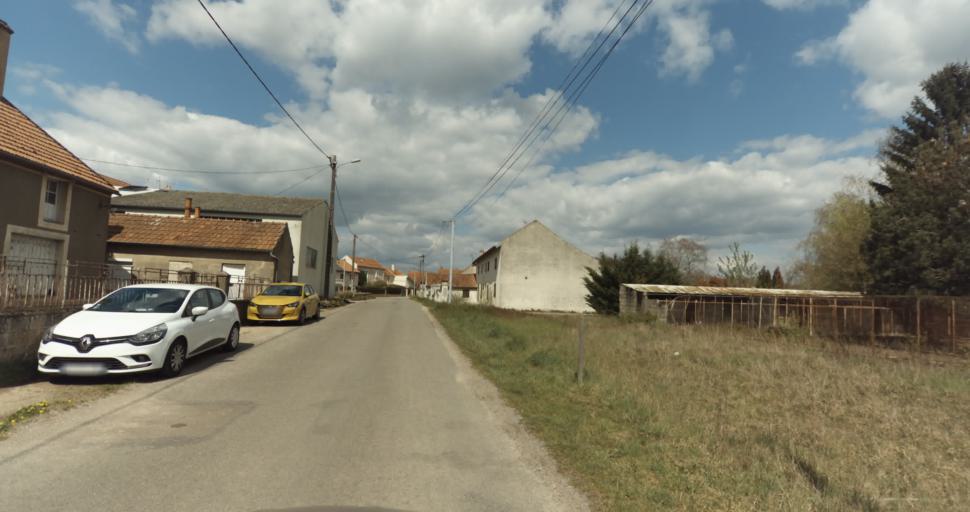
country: FR
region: Bourgogne
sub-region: Departement de la Cote-d'Or
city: Auxonne
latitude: 47.1835
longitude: 5.3914
